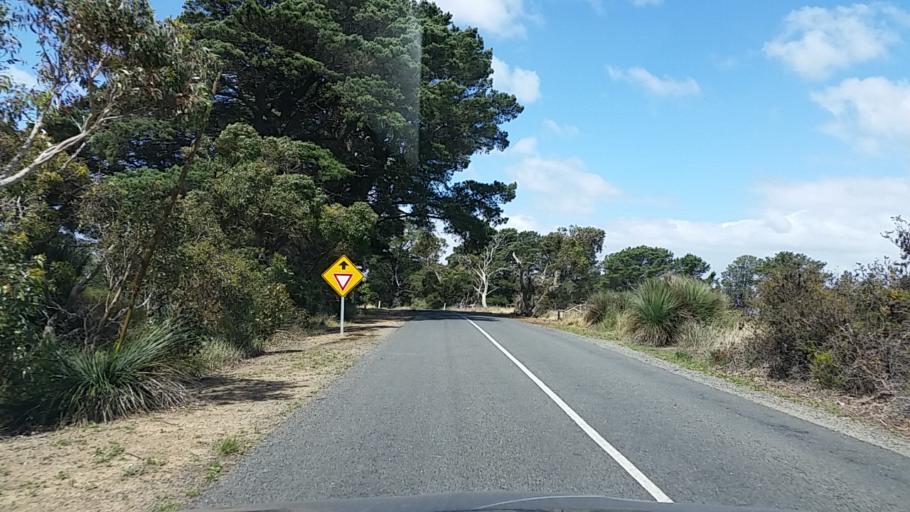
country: AU
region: South Australia
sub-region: Alexandrina
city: Port Elliot
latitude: -35.4544
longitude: 138.6416
